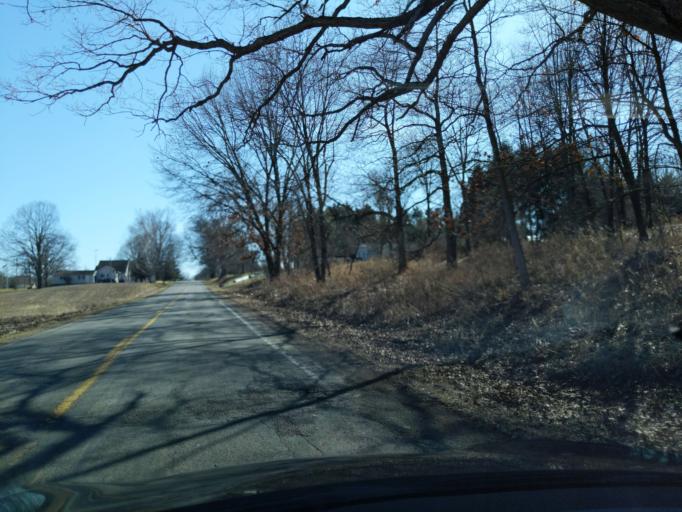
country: US
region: Michigan
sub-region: Ingham County
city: Leslie
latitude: 42.4005
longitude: -84.4433
